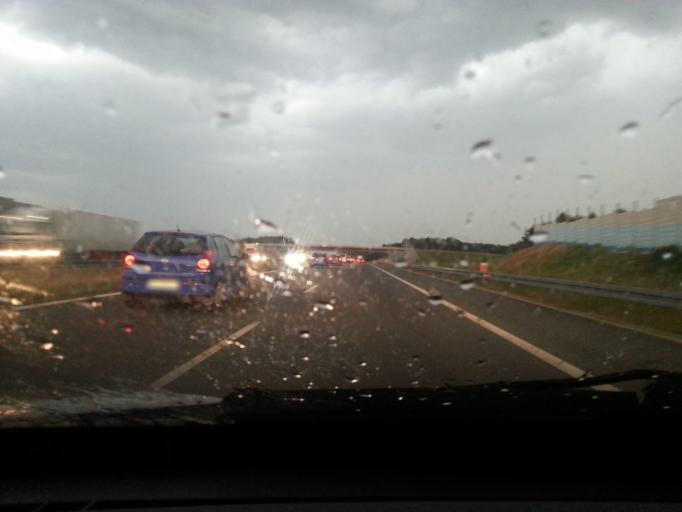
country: PL
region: Lodz Voivodeship
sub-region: powiat Lowicki
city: Lyszkowice
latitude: 51.9669
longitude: 19.8617
